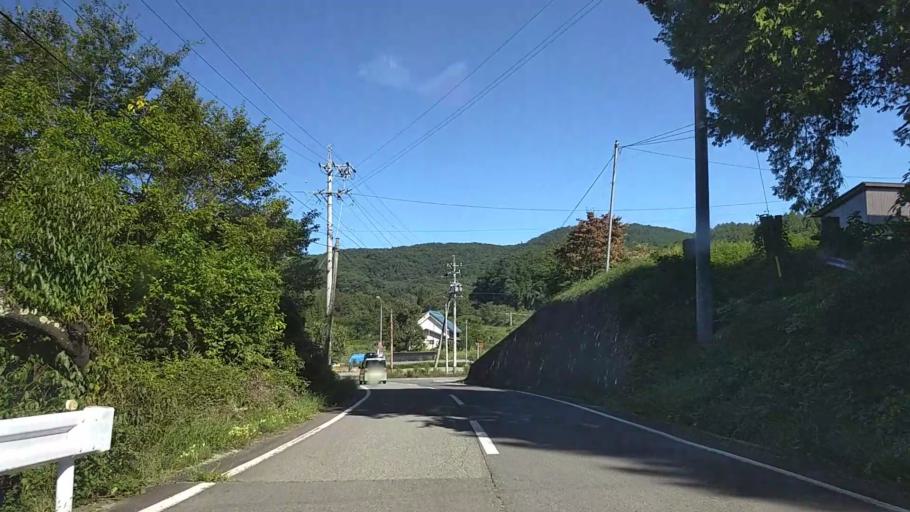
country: JP
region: Nagano
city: Nagano-shi
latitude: 36.6006
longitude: 138.0915
